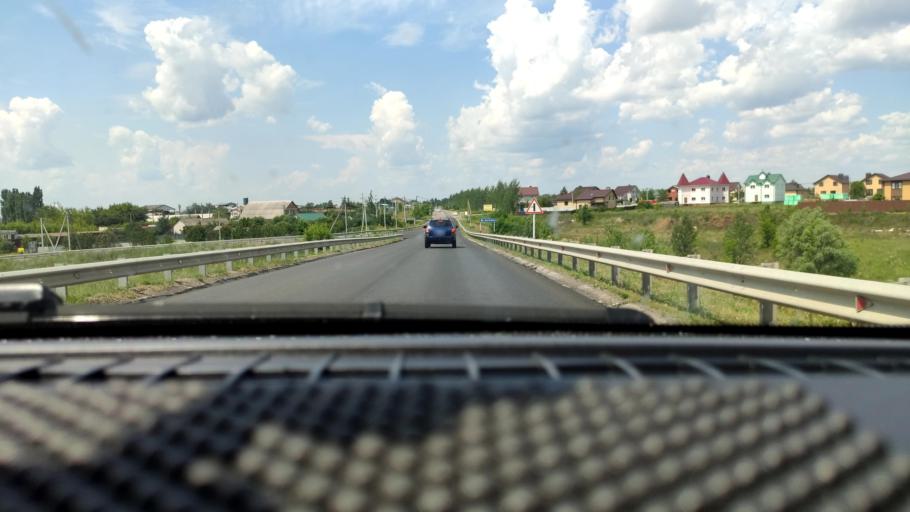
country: RU
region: Voronezj
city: Somovo
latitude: 51.6953
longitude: 39.3837
